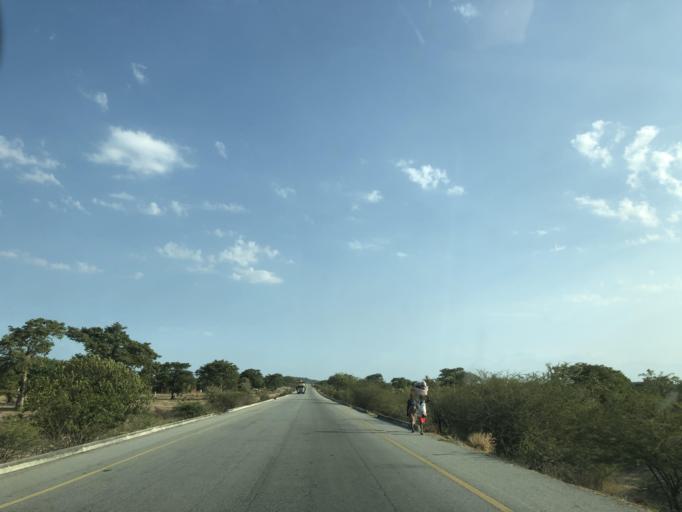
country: AO
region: Benguela
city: Benguela
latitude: -13.2100
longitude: 13.7642
